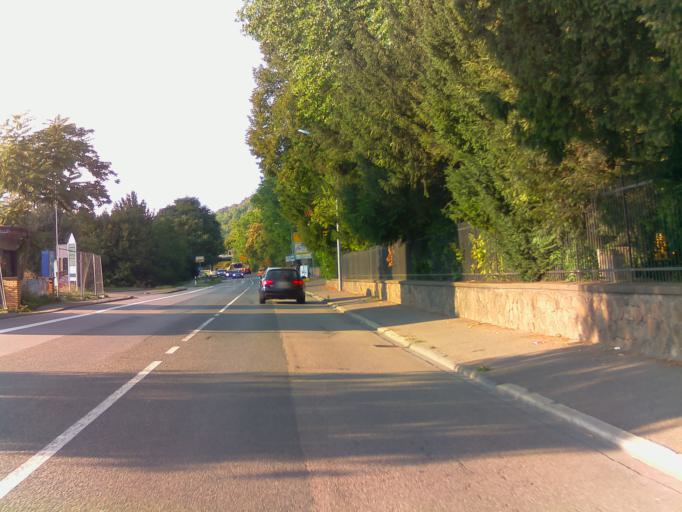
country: DE
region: Baden-Wuerttemberg
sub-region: Karlsruhe Region
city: Weinheim
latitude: 49.5675
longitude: 8.6637
